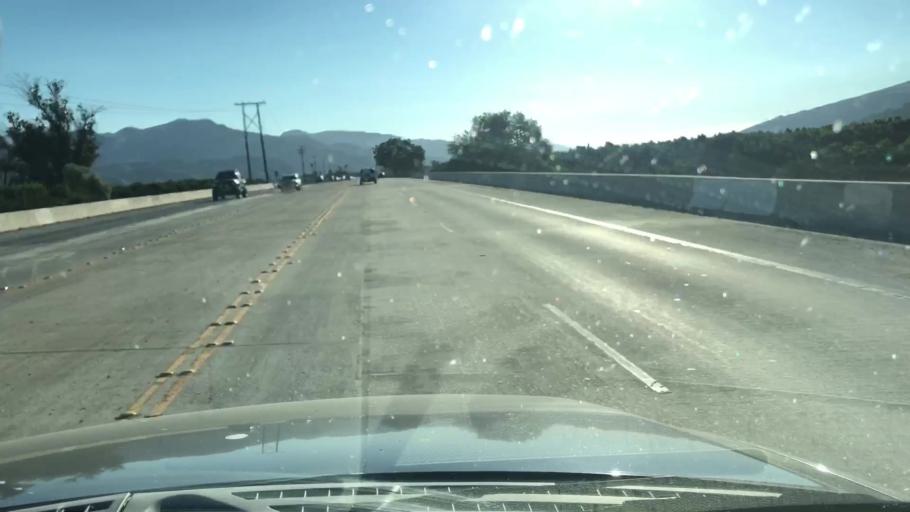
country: US
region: California
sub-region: Ventura County
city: Piru
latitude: 34.4097
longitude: -118.7867
